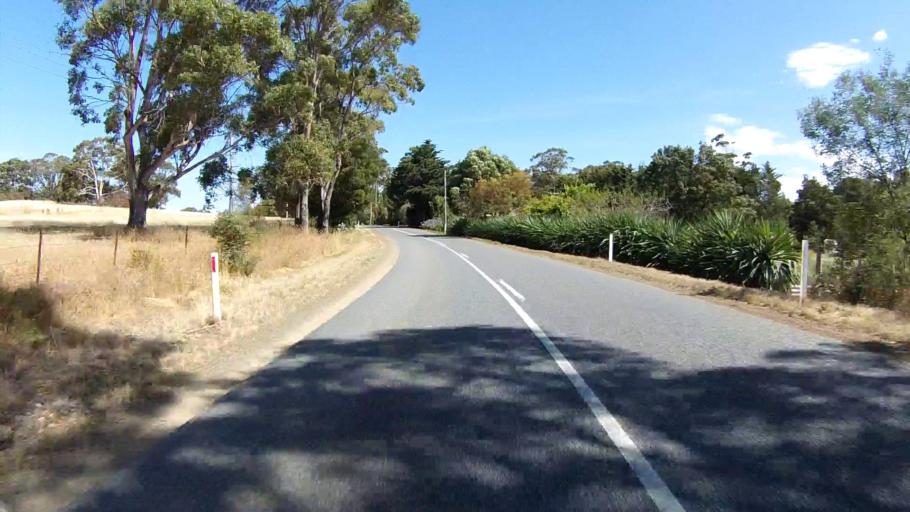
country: AU
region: Tasmania
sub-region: Sorell
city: Sorell
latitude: -42.3072
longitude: 147.9637
